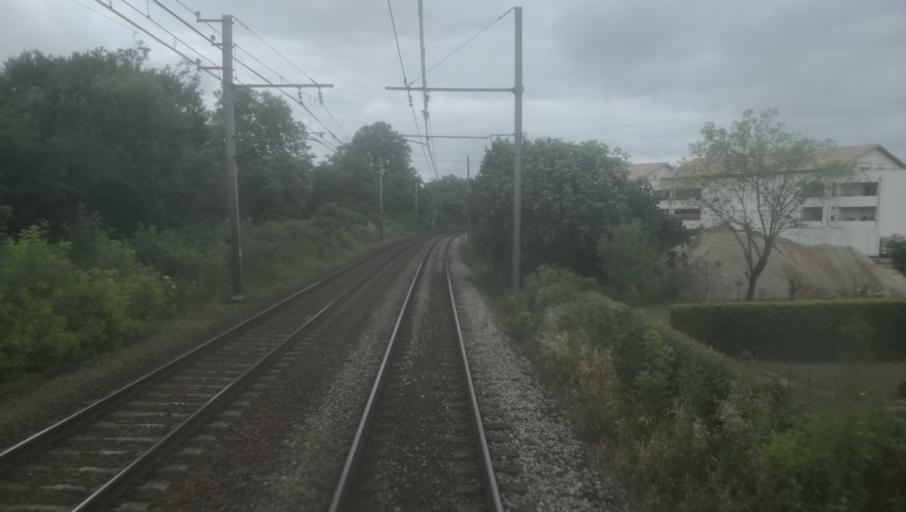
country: FR
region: Midi-Pyrenees
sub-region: Departement de la Haute-Garonne
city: Saint-Jory
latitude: 43.7415
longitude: 1.3683
